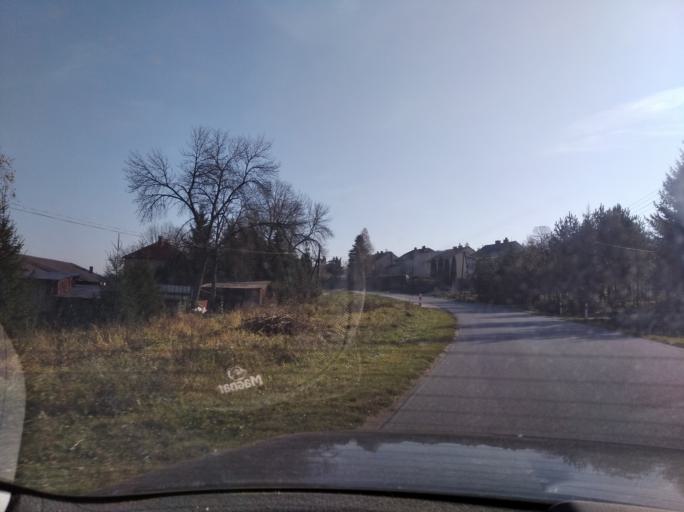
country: PL
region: Subcarpathian Voivodeship
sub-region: Powiat ropczycko-sedziszowski
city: Wielopole Skrzynskie
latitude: 49.9462
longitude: 21.6020
